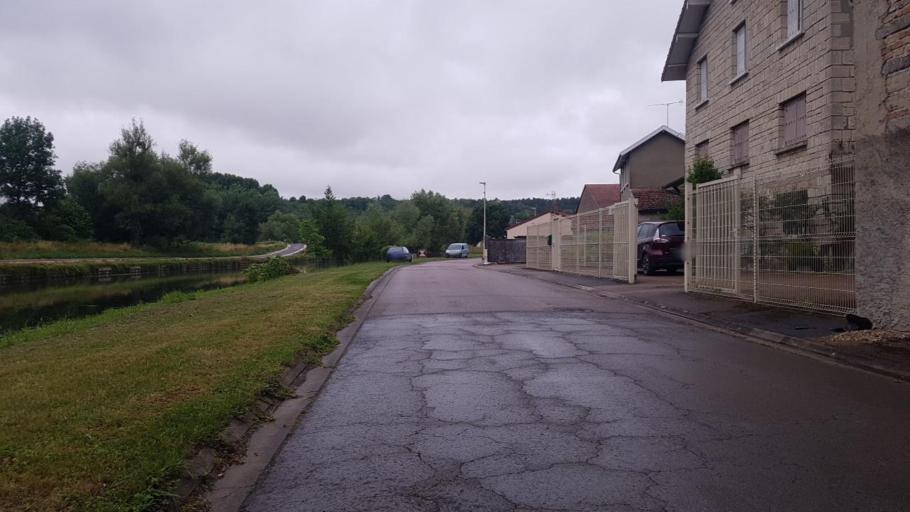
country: FR
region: Champagne-Ardenne
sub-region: Departement de la Marne
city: Vitry-le-Francois
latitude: 48.7546
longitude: 4.5697
